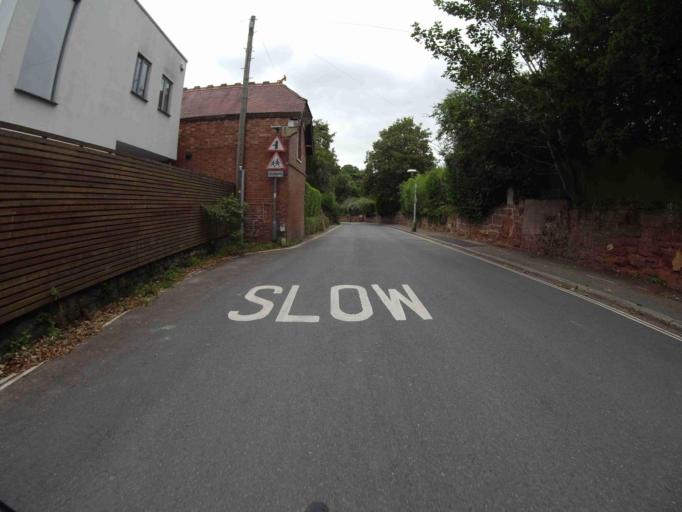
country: GB
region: England
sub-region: Devon
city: Exeter
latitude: 50.7175
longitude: -3.5157
